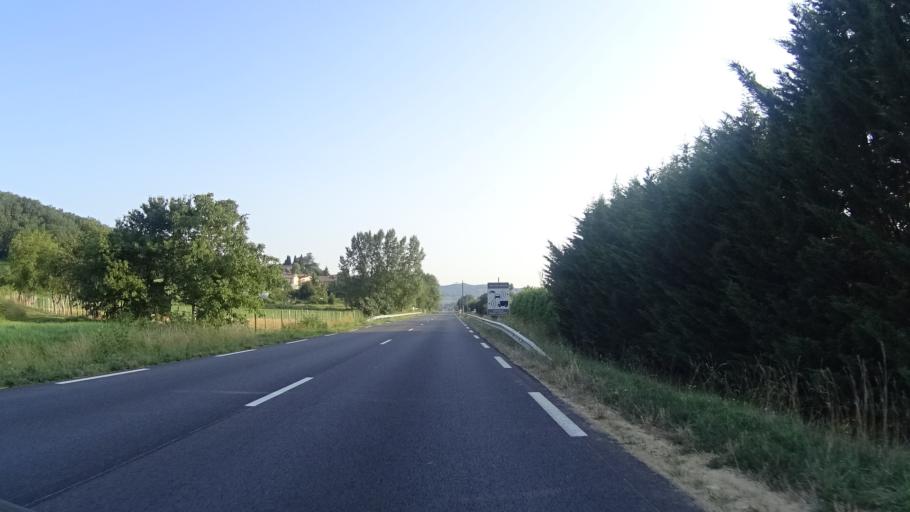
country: FR
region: Midi-Pyrenees
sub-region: Departement de l'Ariege
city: Mirepoix
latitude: 43.0307
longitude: 1.8968
